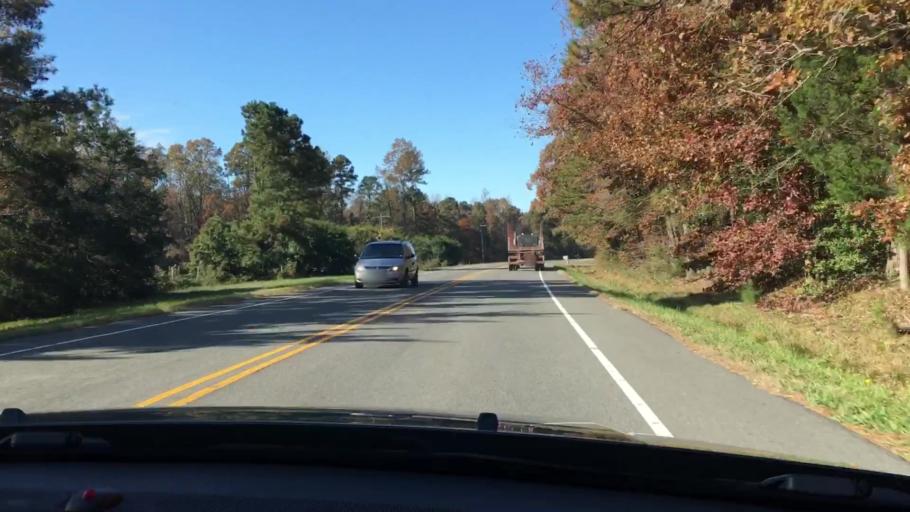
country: US
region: Virginia
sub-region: King William County
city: Central Garage
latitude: 37.7787
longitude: -77.1653
